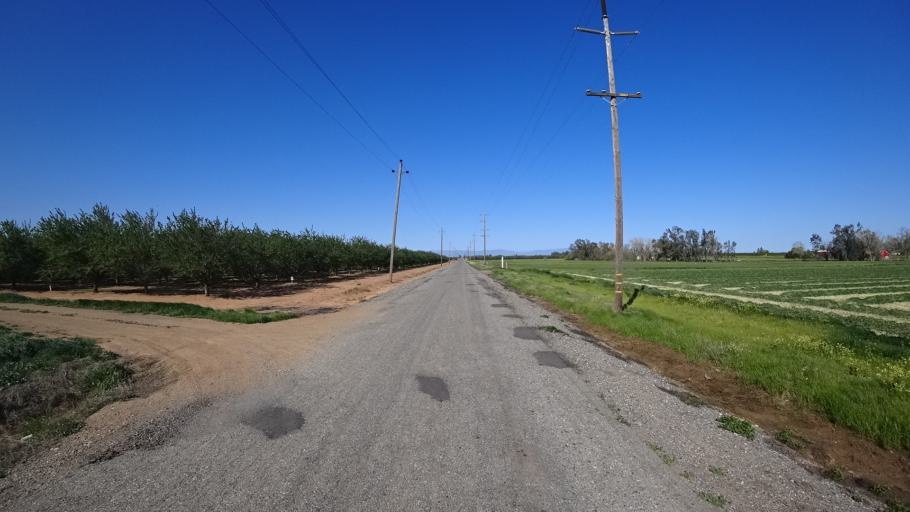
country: US
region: California
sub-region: Glenn County
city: Hamilton City
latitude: 39.7756
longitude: -122.0616
